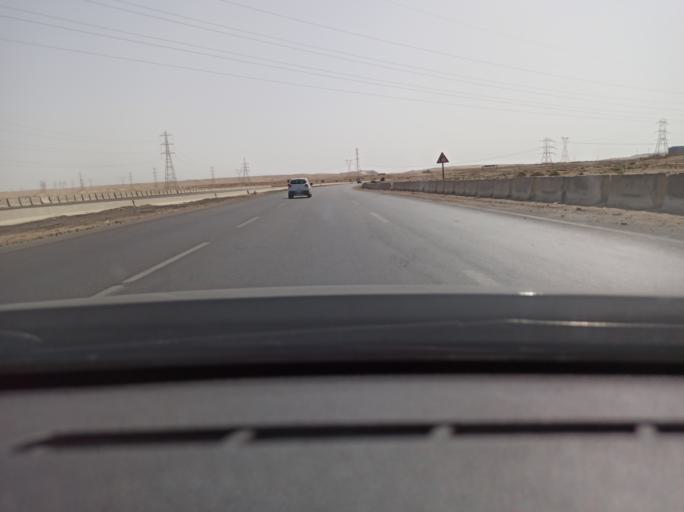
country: EG
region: Muhafazat al Qahirah
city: Halwan
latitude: 29.7663
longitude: 31.3944
